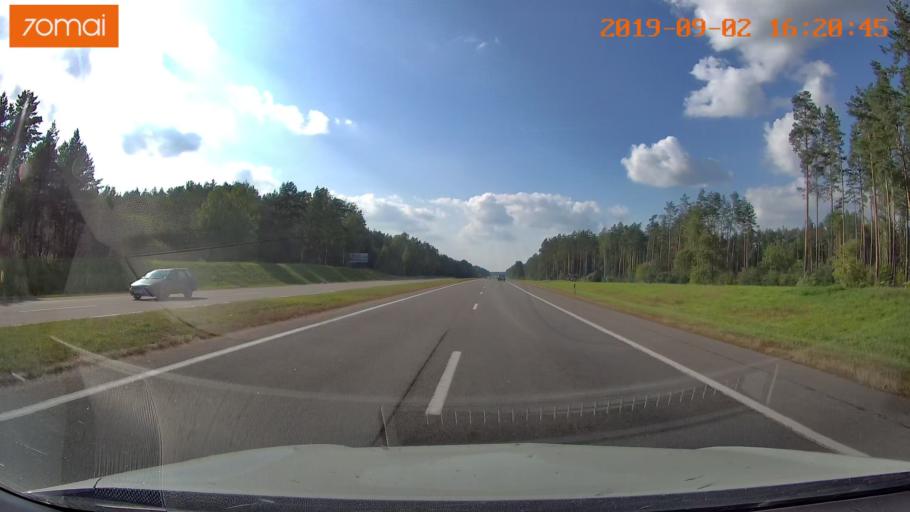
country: BY
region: Minsk
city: Chervyen'
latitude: 53.7253
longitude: 28.3710
